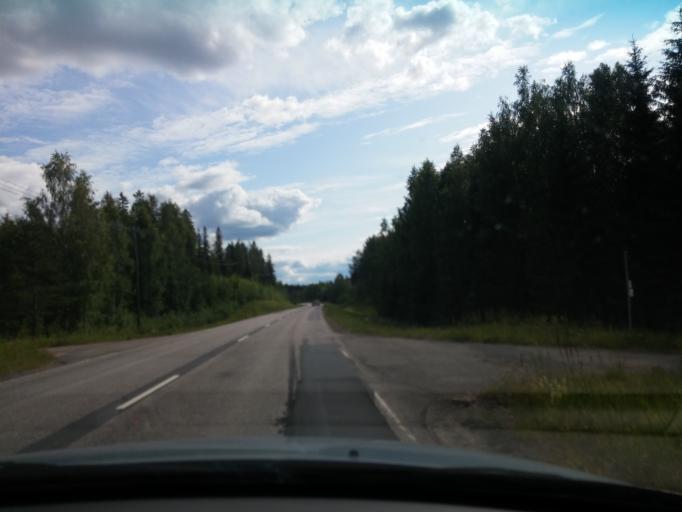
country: FI
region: Central Finland
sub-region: Keuruu
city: Multia
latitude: 62.3561
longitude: 24.7400
